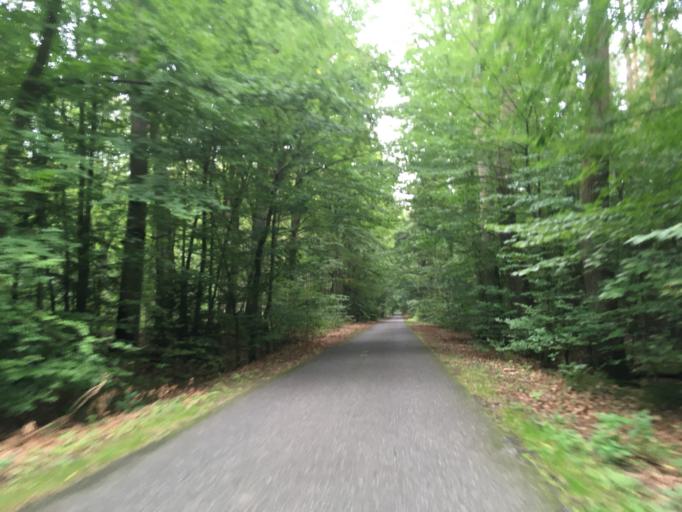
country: DE
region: Brandenburg
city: Gransee
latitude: 53.0649
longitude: 13.1968
